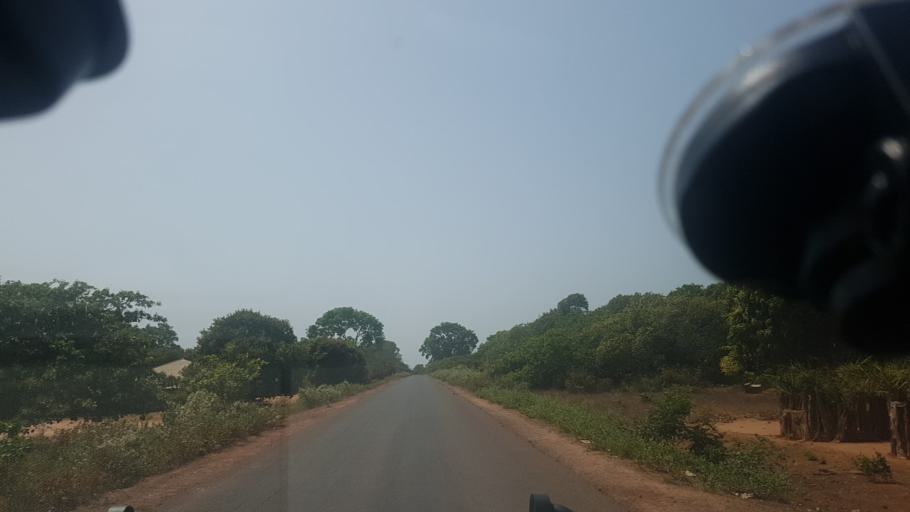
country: GW
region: Cacheu
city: Cacheu
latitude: 12.4114
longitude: -16.0669
